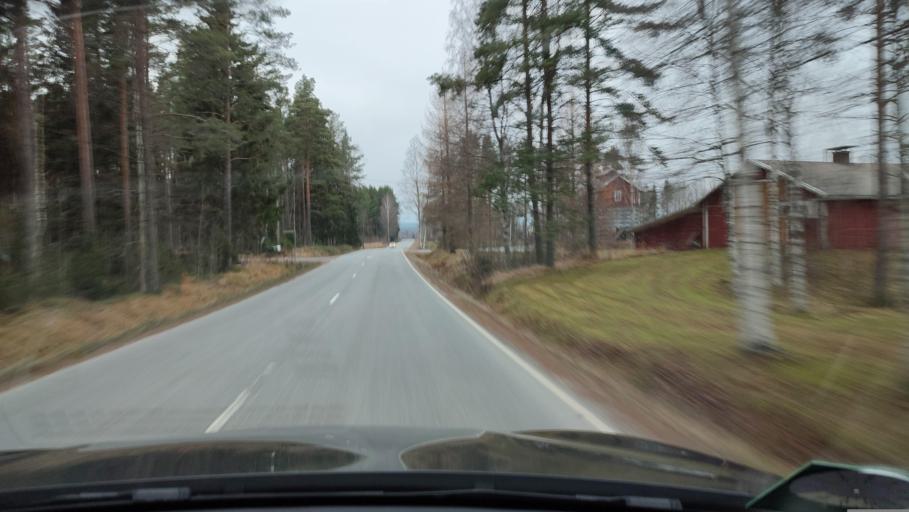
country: FI
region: Southern Ostrobothnia
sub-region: Suupohja
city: Karijoki
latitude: 62.2637
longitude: 21.7304
